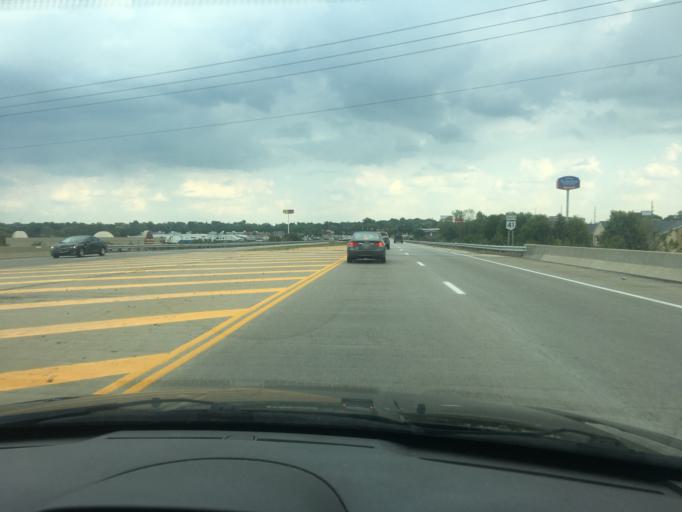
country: US
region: Ohio
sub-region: Clark County
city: Springfield
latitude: 39.9429
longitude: -83.8404
